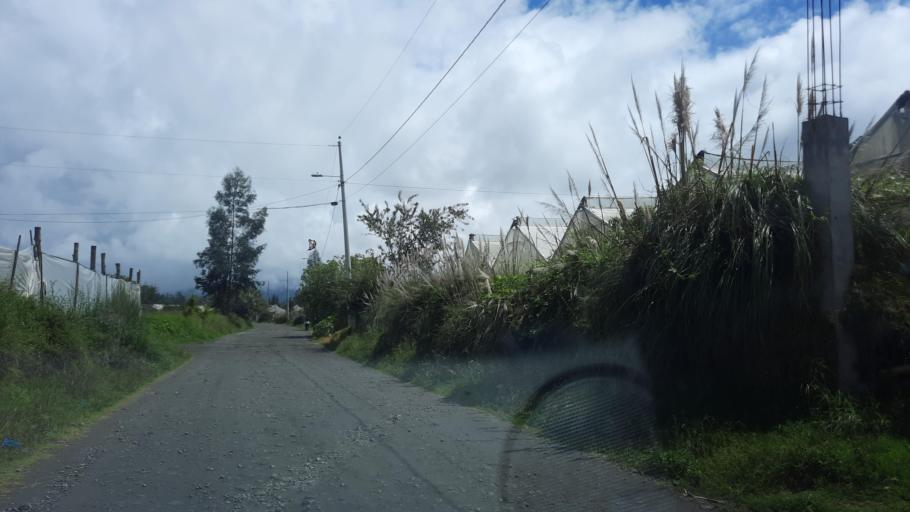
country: EC
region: Chimborazo
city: Riobamba
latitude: -1.6901
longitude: -78.6655
